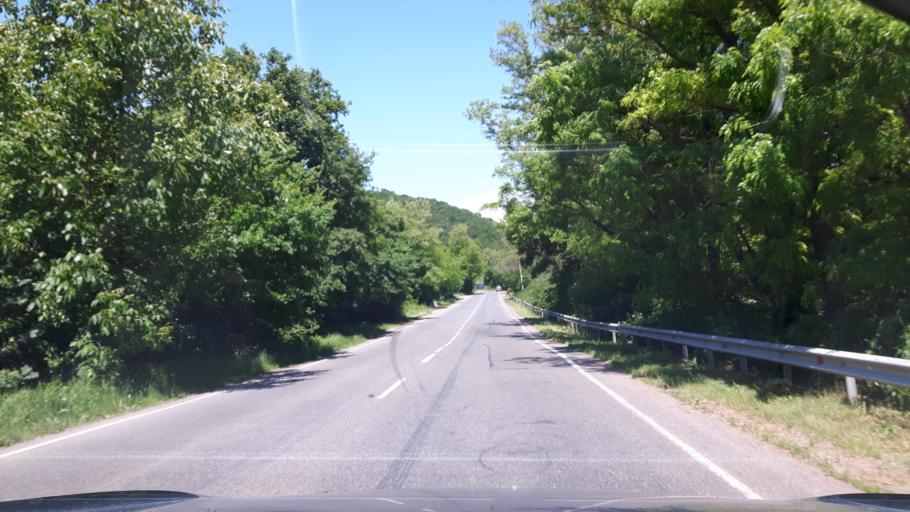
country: GE
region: Kakheti
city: Sighnaghi
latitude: 41.6389
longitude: 45.8274
